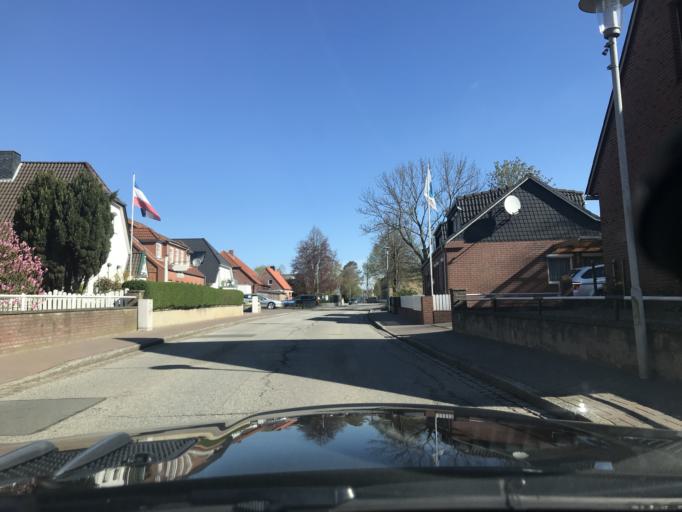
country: DE
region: Schleswig-Holstein
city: Grossenbrode
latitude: 54.3736
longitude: 11.0849
